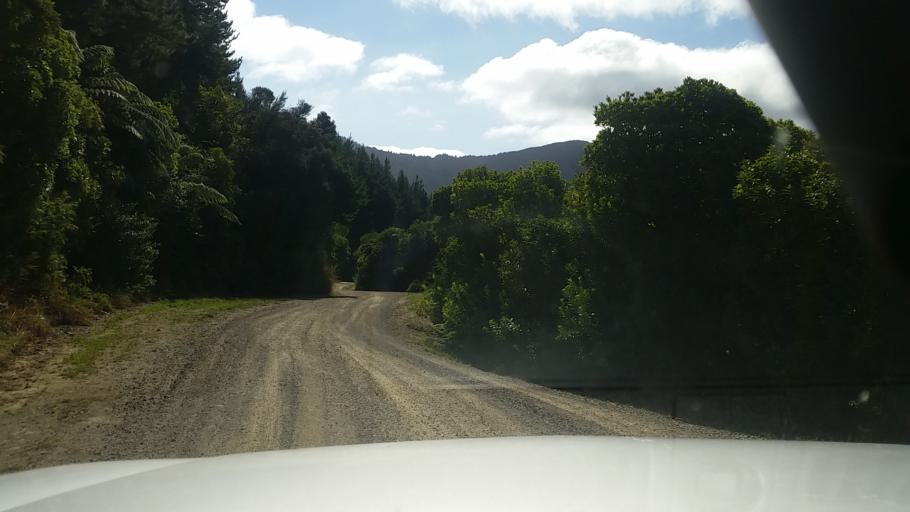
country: NZ
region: Marlborough
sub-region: Marlborough District
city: Picton
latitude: -41.2914
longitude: 174.1680
